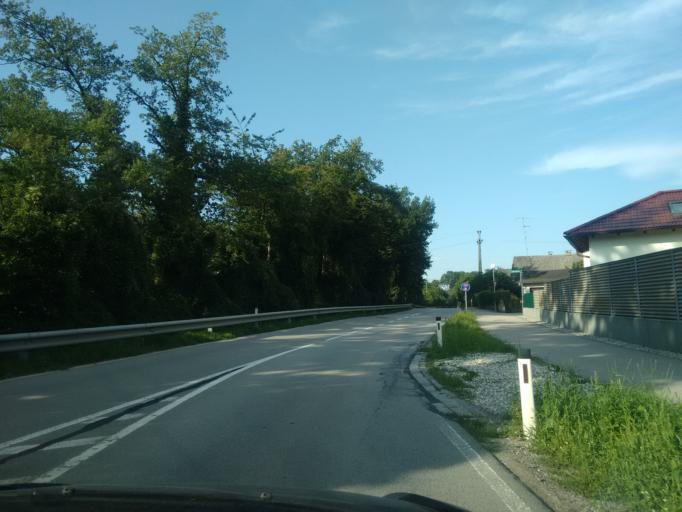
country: DE
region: Bavaria
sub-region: Lower Bavaria
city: Kirchdorf am Inn
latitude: 48.2296
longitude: 13.0078
